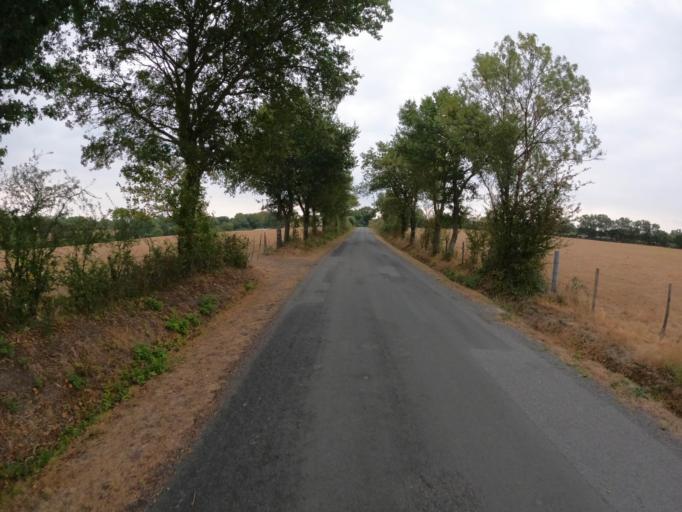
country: FR
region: Pays de la Loire
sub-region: Departement de la Vendee
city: Saint-Georges-de-Montaigu
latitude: 46.9710
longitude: -1.2820
